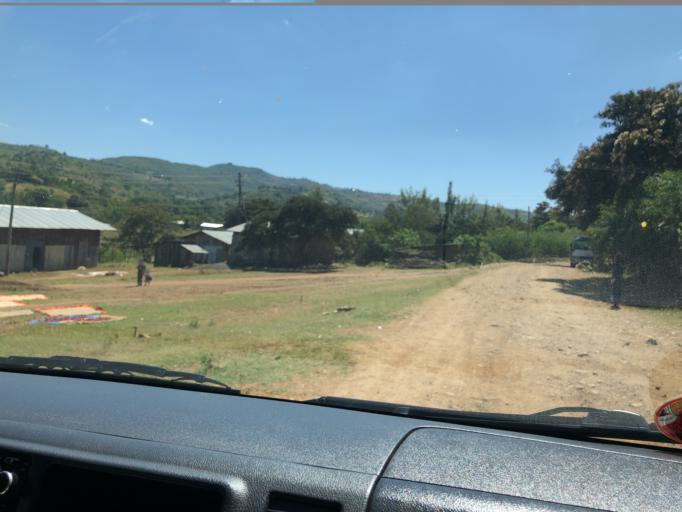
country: ET
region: Amhara
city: Werota
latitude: 11.9210
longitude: 37.7872
